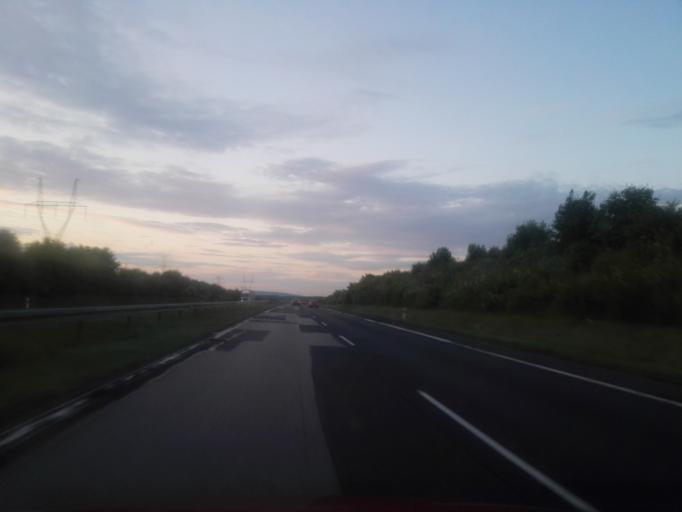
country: PL
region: Lodz Voivodeship
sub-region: Powiat radomszczanski
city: Radomsko
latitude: 51.0908
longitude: 19.3769
